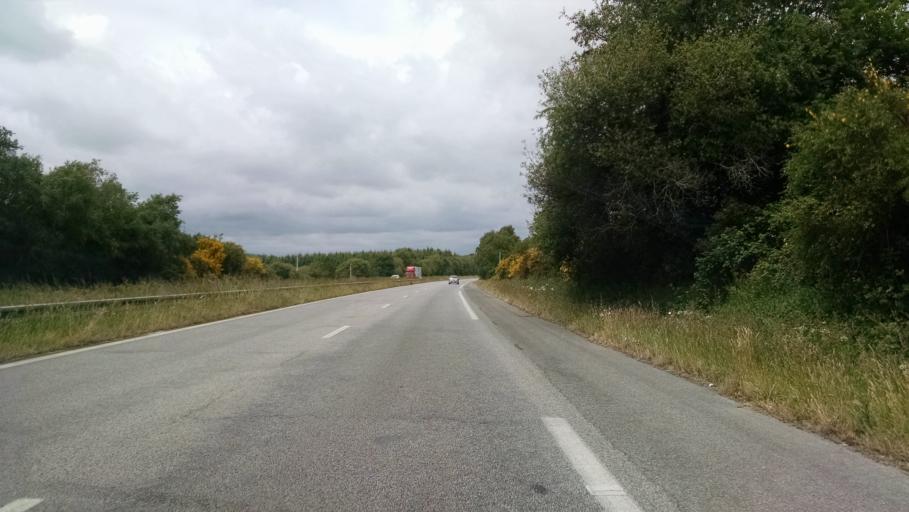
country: FR
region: Brittany
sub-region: Departement du Morbihan
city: Gestel
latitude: 47.7960
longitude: -3.4526
